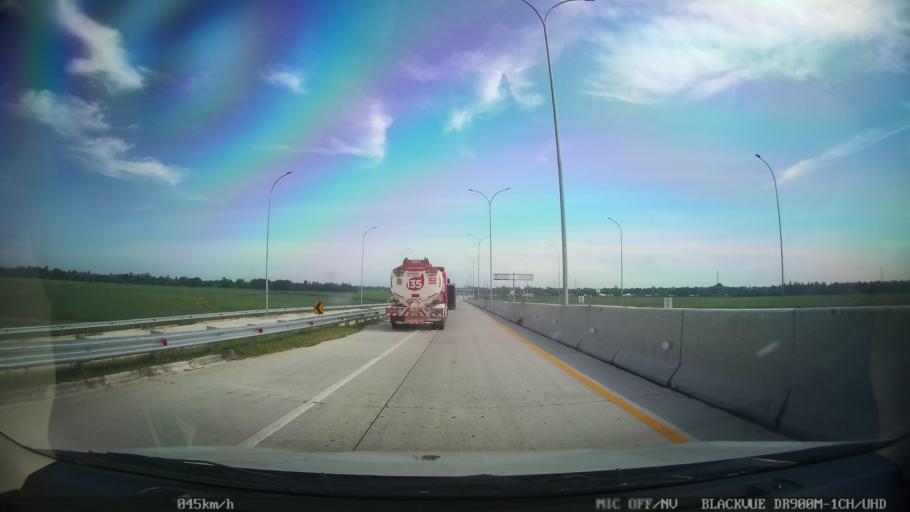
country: ID
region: North Sumatra
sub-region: Kabupaten Langkat
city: Stabat
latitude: 3.7138
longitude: 98.4936
